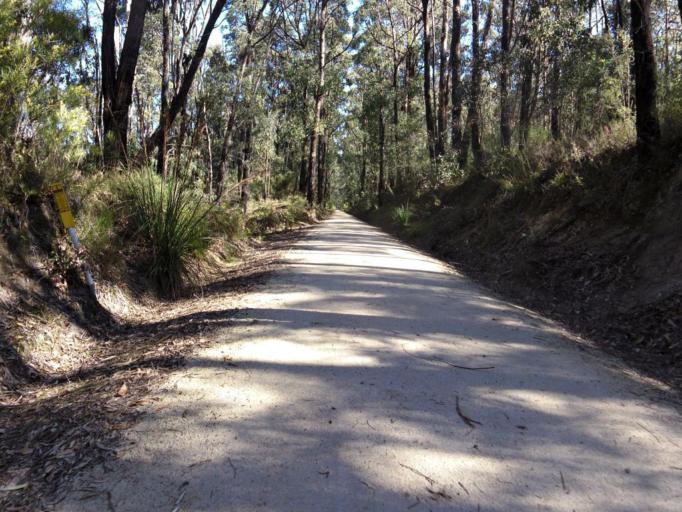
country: AU
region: Victoria
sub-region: Latrobe
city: Moe
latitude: -38.3833
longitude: 146.1914
